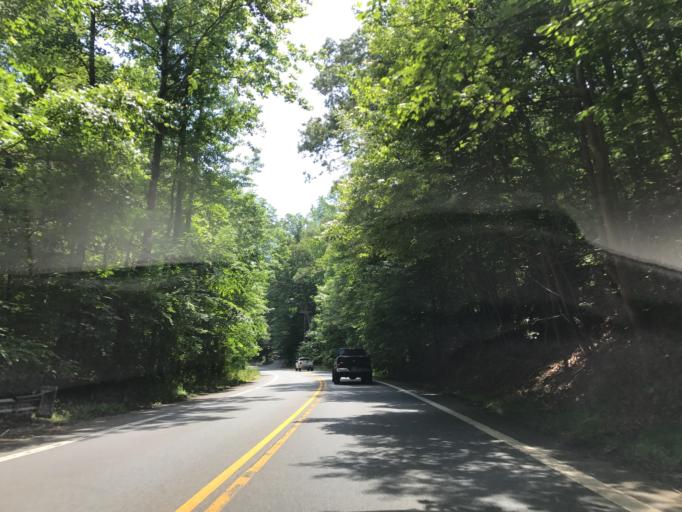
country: US
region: Maryland
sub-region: Anne Arundel County
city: Crownsville
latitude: 38.9891
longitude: -76.6060
